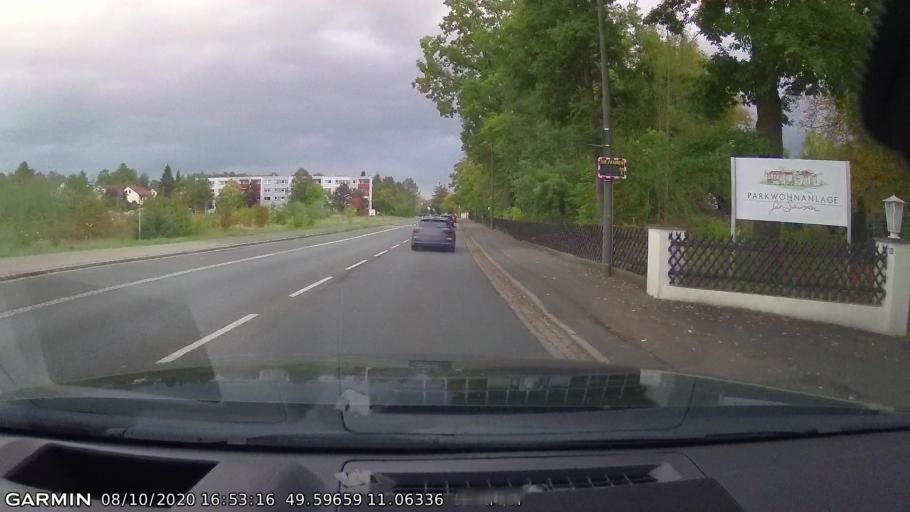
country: DE
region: Bavaria
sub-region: Regierungsbezirk Mittelfranken
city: Uttenreuth
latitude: 49.5966
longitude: 11.0632
